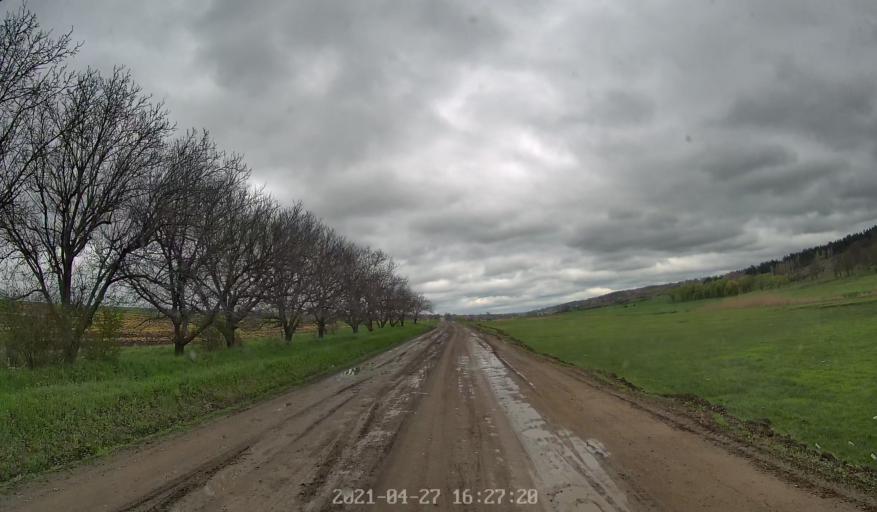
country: MD
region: Chisinau
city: Singera
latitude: 46.9759
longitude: 29.0332
